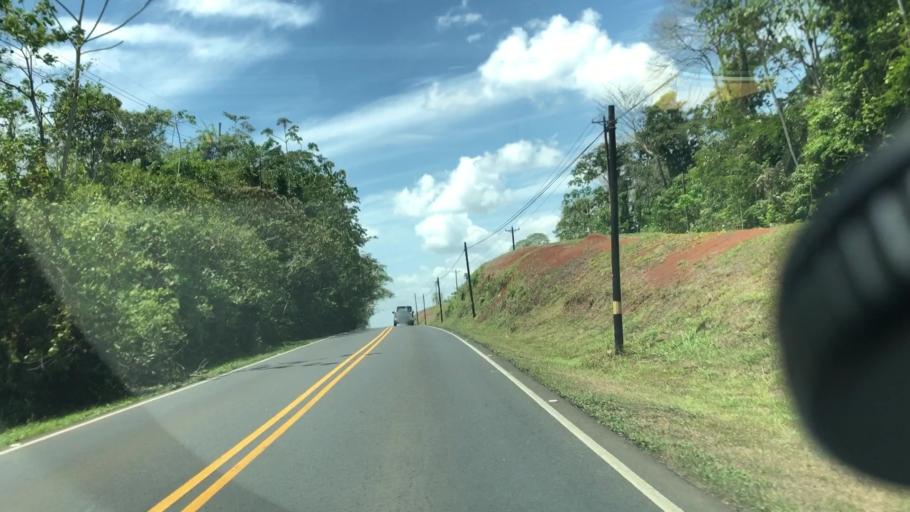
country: CR
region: Alajuela
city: Pital
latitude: 10.4535
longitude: -84.3807
